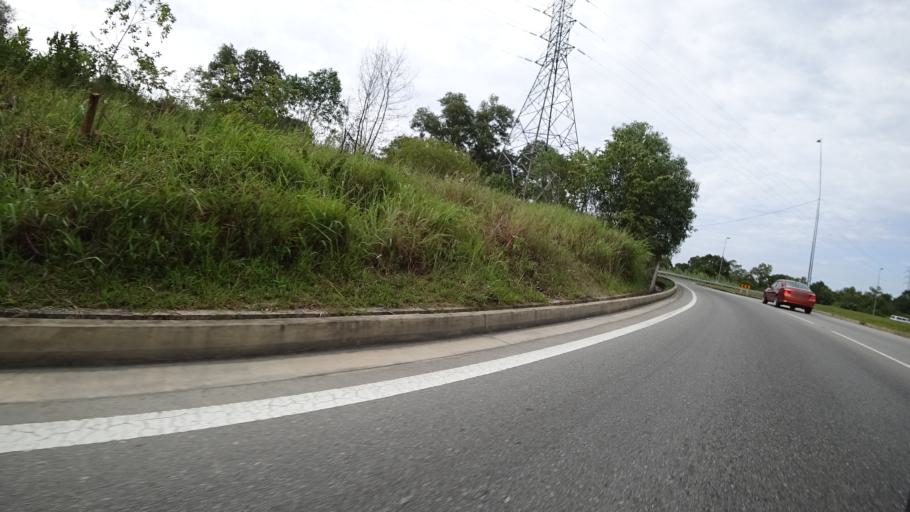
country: BN
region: Brunei and Muara
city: Bandar Seri Begawan
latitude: 4.9329
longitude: 114.8836
